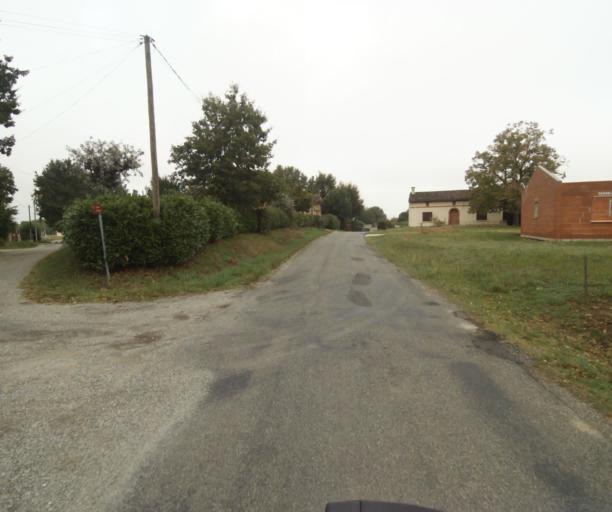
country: FR
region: Midi-Pyrenees
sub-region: Departement du Tarn-et-Garonne
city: Labastide-Saint-Pierre
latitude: 43.8843
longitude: 1.3806
